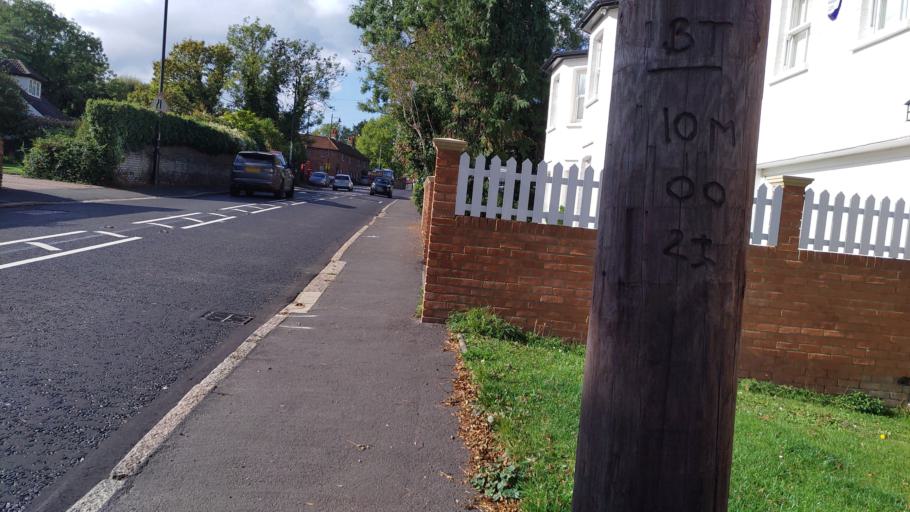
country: GB
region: England
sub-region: Hertfordshire
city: Potters Bar
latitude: 51.7040
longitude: -0.1492
